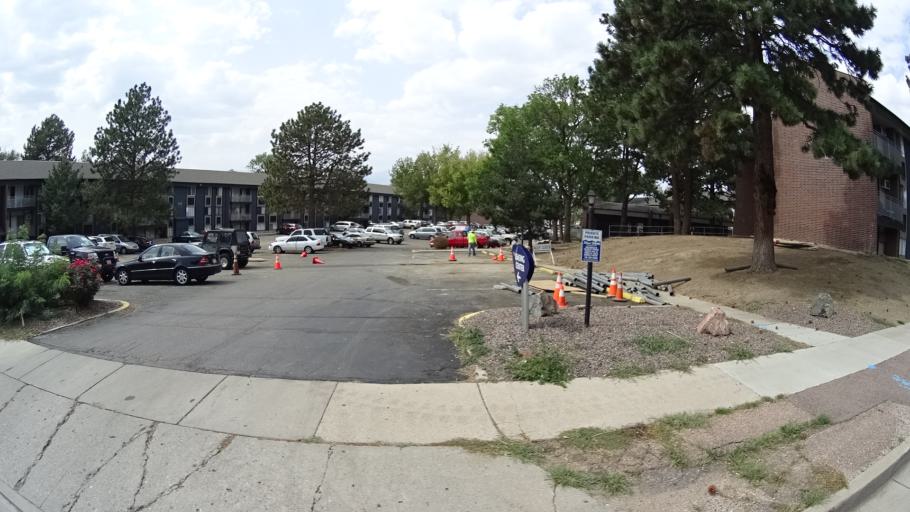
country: US
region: Colorado
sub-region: El Paso County
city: Cimarron Hills
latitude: 38.8567
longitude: -104.7480
